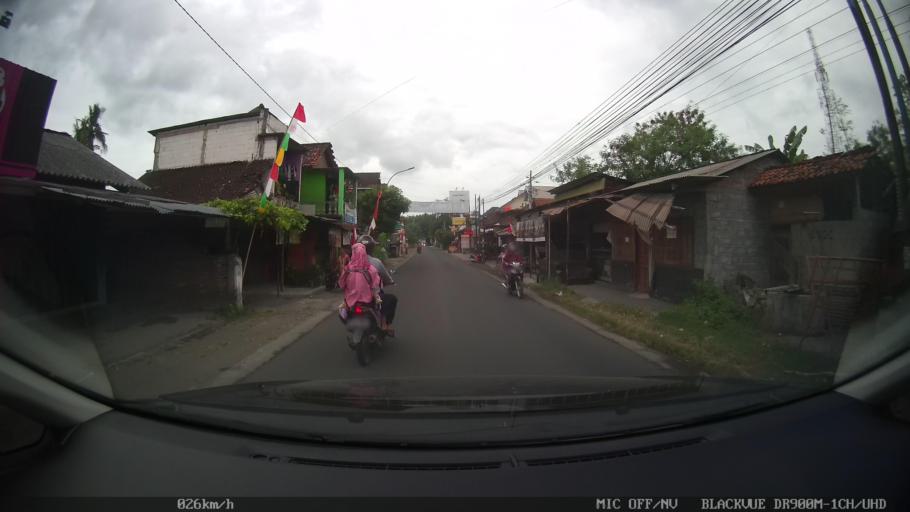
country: ID
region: Daerah Istimewa Yogyakarta
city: Sewon
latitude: -7.8623
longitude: 110.4086
